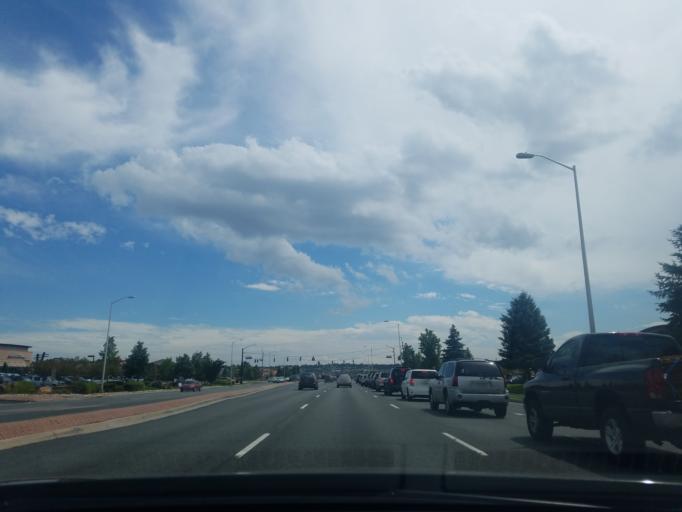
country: US
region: Colorado
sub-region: El Paso County
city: Air Force Academy
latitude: 38.9385
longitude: -104.7986
